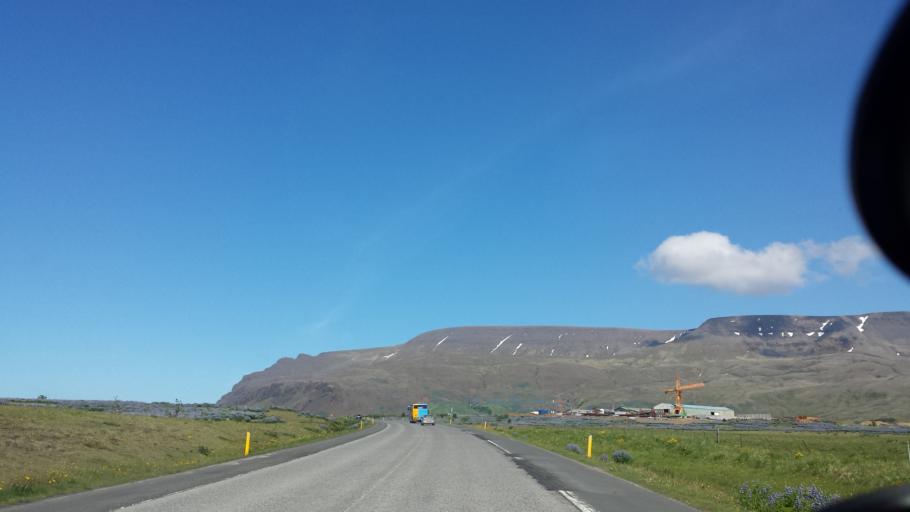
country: IS
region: Capital Region
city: Mosfellsbaer
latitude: 64.1896
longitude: -21.6872
